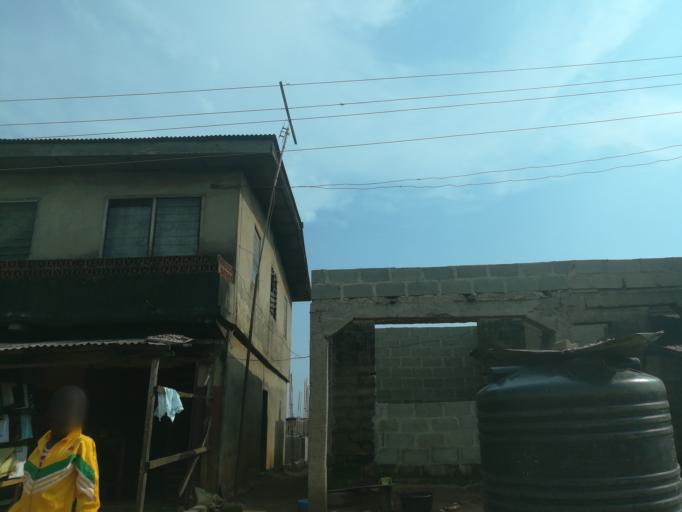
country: NG
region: Lagos
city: Ikorodu
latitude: 6.6628
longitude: 3.6714
